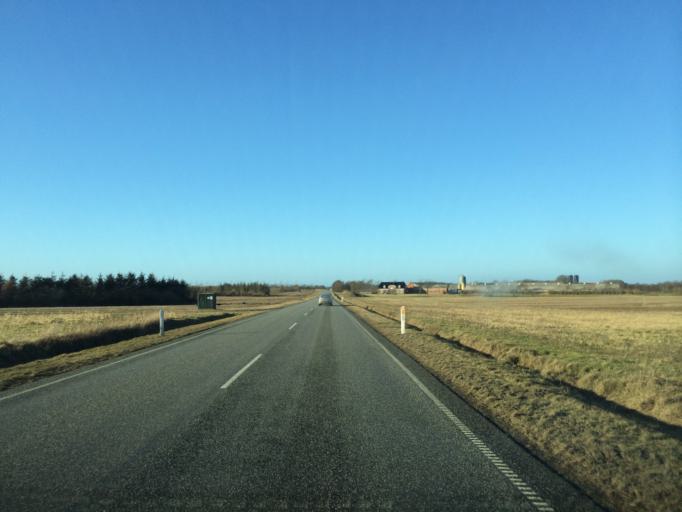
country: DK
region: Central Jutland
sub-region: Ringkobing-Skjern Kommune
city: Ringkobing
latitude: 56.0989
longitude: 8.3321
